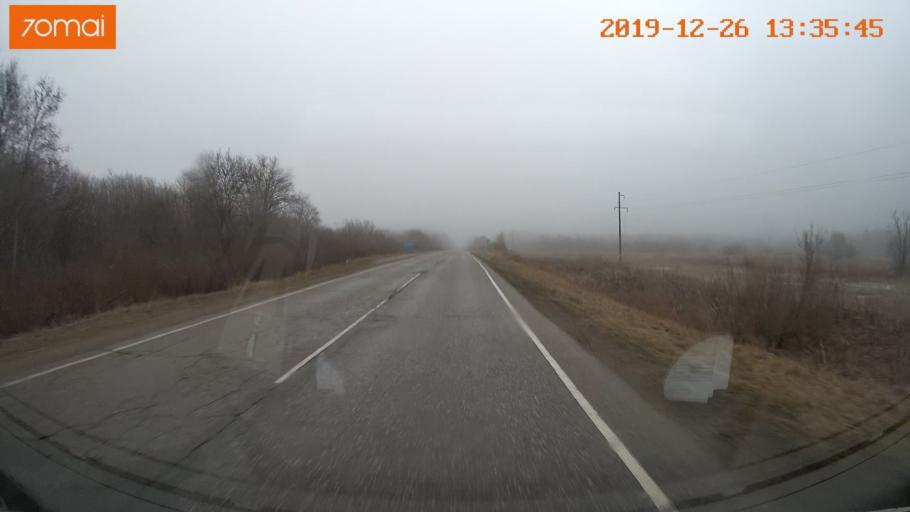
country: RU
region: Vologda
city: Sheksna
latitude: 58.7903
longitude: 38.3445
